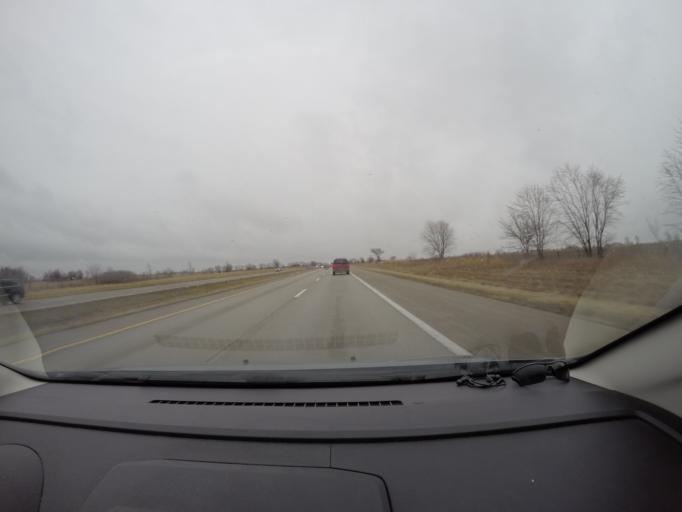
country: US
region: Missouri
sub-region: Callaway County
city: Fulton
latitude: 38.9161
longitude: -91.7408
